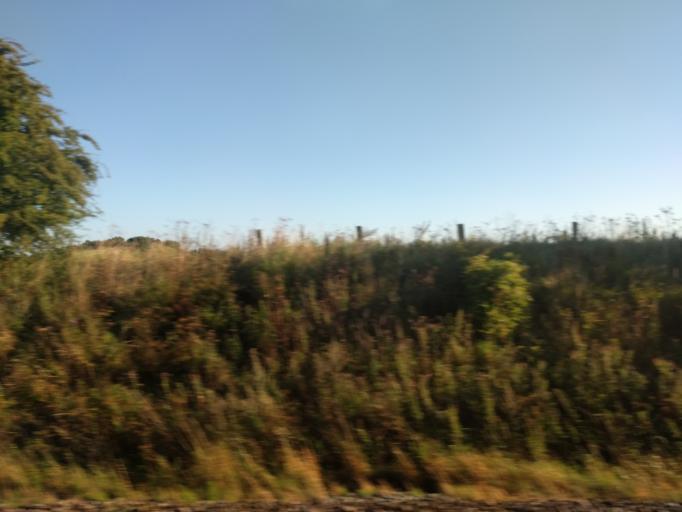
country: DK
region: Zealand
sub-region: Slagelse Kommune
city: Slagelse
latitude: 55.4087
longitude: 11.4444
